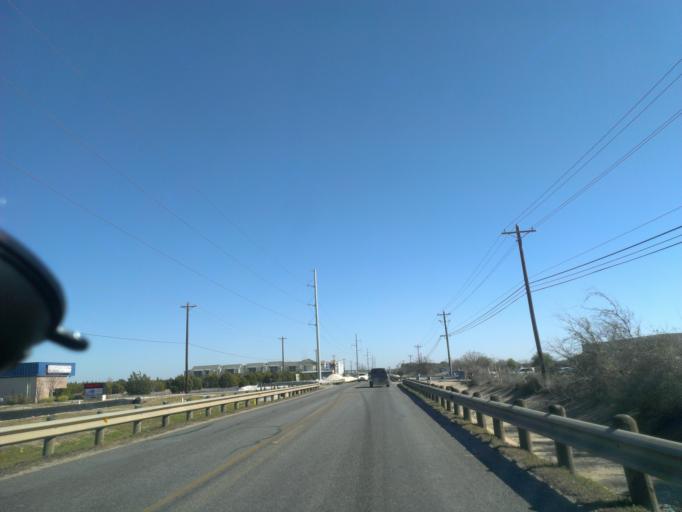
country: US
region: Texas
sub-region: Williamson County
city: Leander
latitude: 30.5777
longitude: -97.8687
